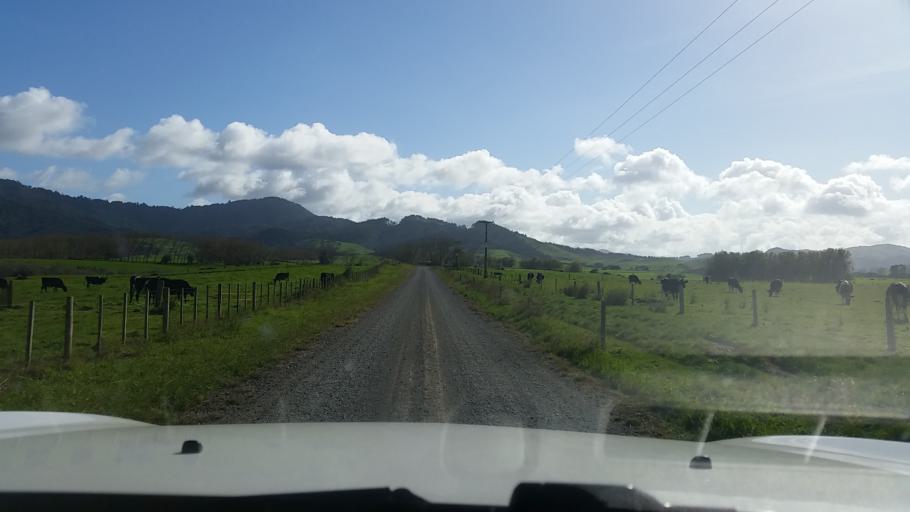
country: NZ
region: Waikato
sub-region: Hauraki District
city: Ngatea
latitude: -37.5110
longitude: 175.4085
